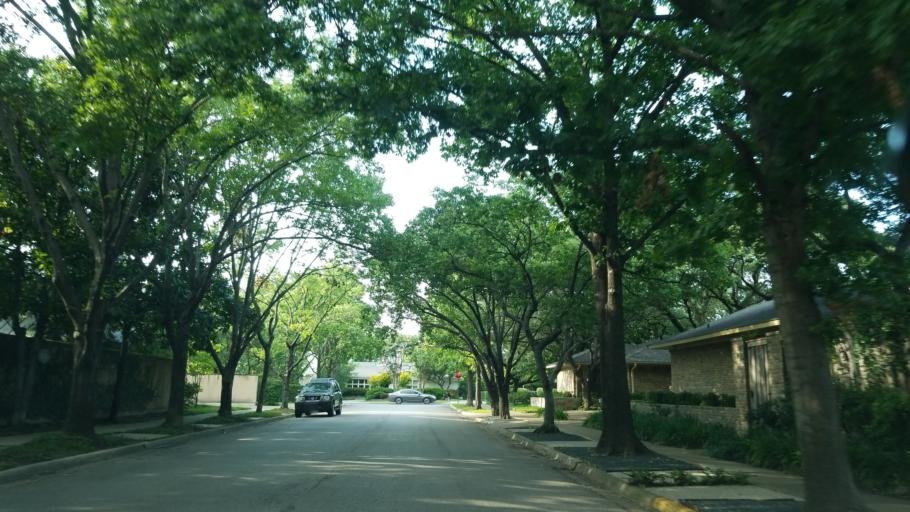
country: US
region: Texas
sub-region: Dallas County
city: Highland Park
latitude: 32.8359
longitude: -96.7964
